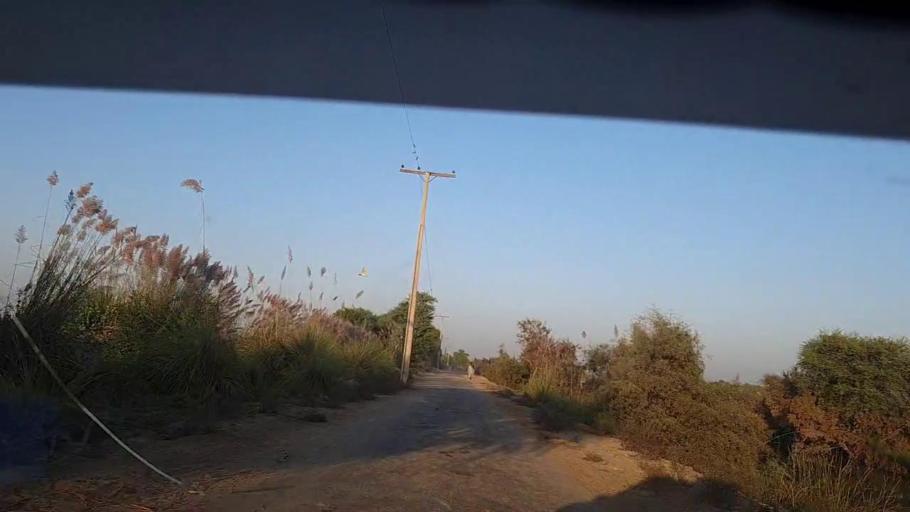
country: PK
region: Sindh
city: Ratodero
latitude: 27.8955
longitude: 68.2264
